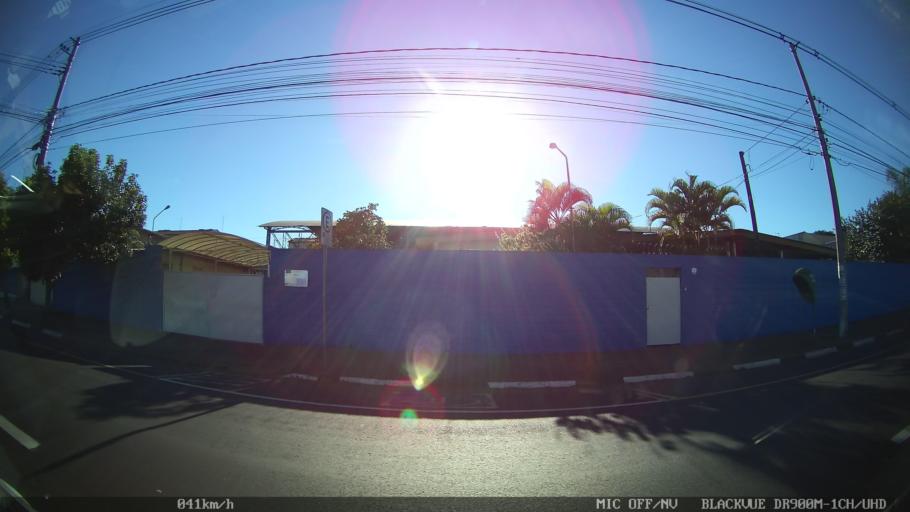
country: BR
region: Sao Paulo
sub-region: Franca
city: Franca
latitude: -20.5743
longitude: -47.3893
